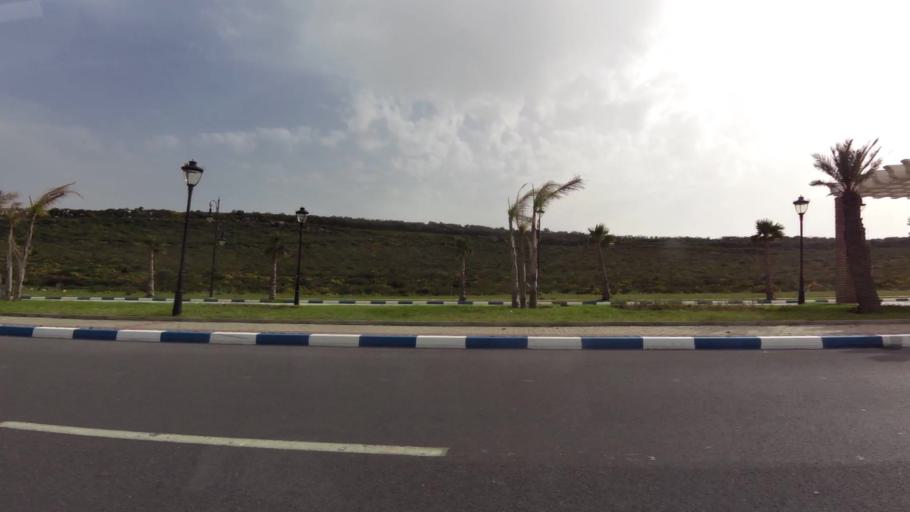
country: MA
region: Tanger-Tetouan
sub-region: Tanger-Assilah
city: Boukhalef
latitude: 35.6976
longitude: -5.9267
